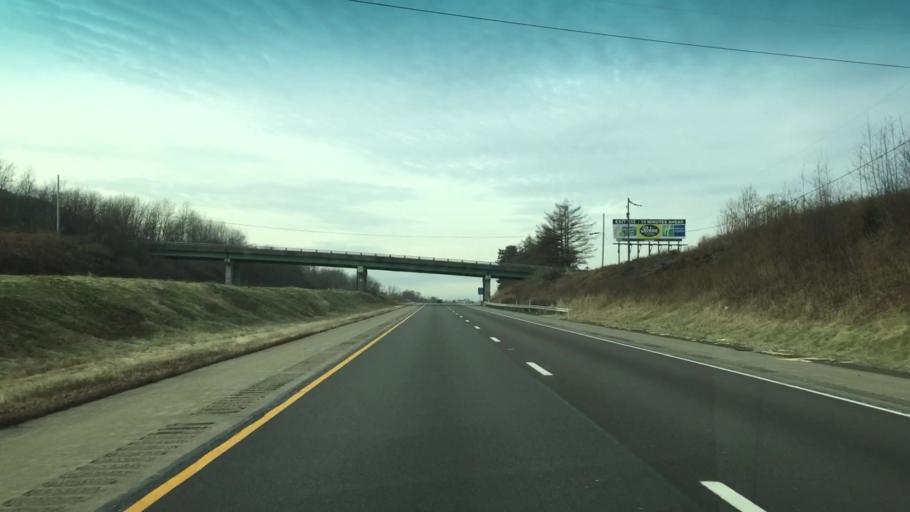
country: US
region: Pennsylvania
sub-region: Luzerne County
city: Nescopeck
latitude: 41.0103
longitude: -76.2347
